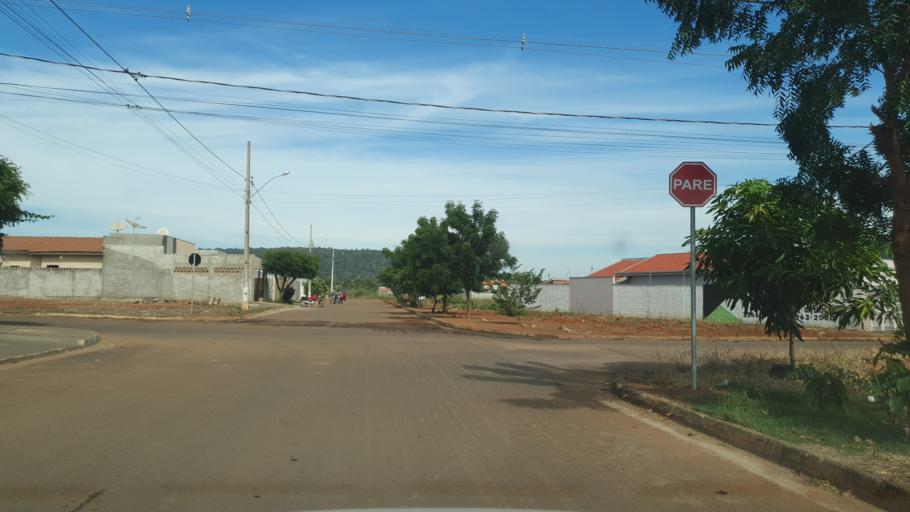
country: BR
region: Mato Grosso
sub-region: Pontes E Lacerda
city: Pontes e Lacerda
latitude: -15.2492
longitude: -59.3193
